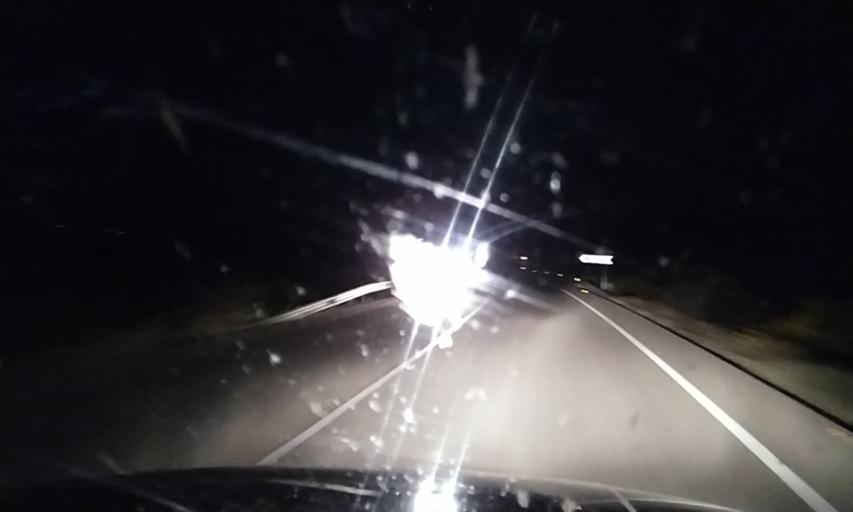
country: ES
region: Extremadura
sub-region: Provincia de Caceres
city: Moraleja
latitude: 40.1061
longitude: -6.6747
